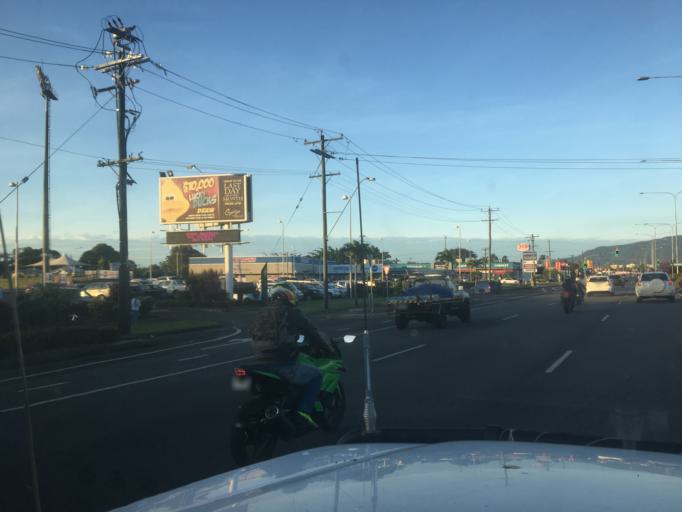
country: AU
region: Queensland
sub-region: Cairns
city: Woree
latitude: -16.9370
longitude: 145.7496
